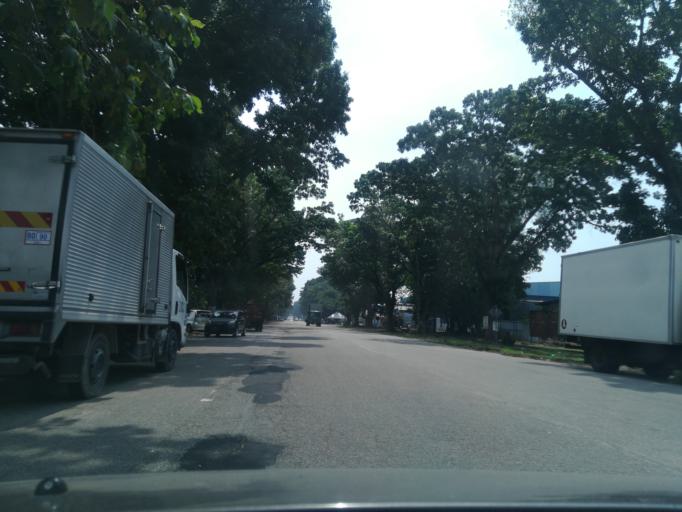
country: MY
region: Kedah
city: Kulim
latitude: 5.4056
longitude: 100.5539
